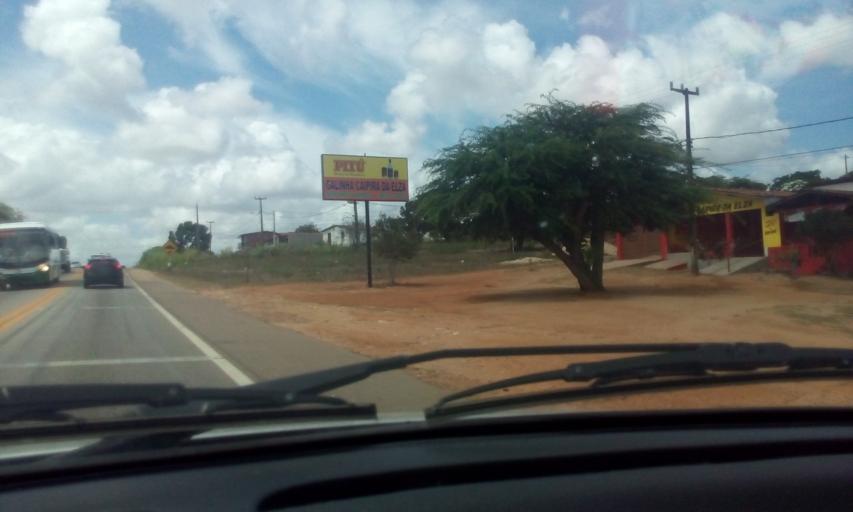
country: BR
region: Rio Grande do Norte
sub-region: Macaiba
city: Macaiba
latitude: -5.9321
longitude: -35.5444
